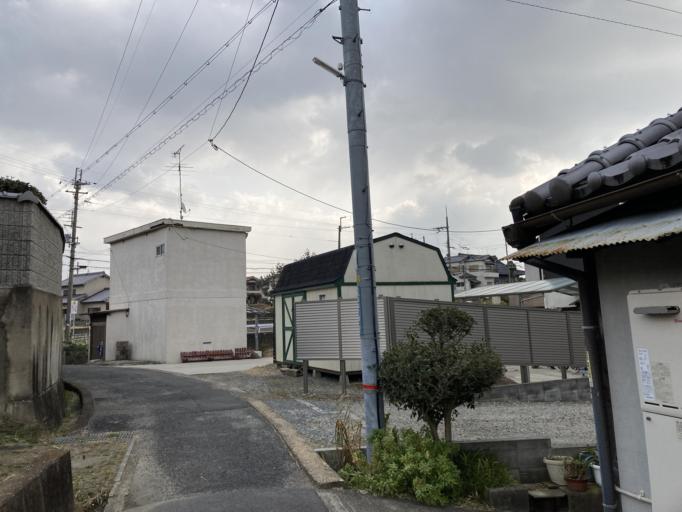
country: JP
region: Nara
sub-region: Ikoma-shi
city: Ikoma
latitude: 34.6093
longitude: 135.7191
